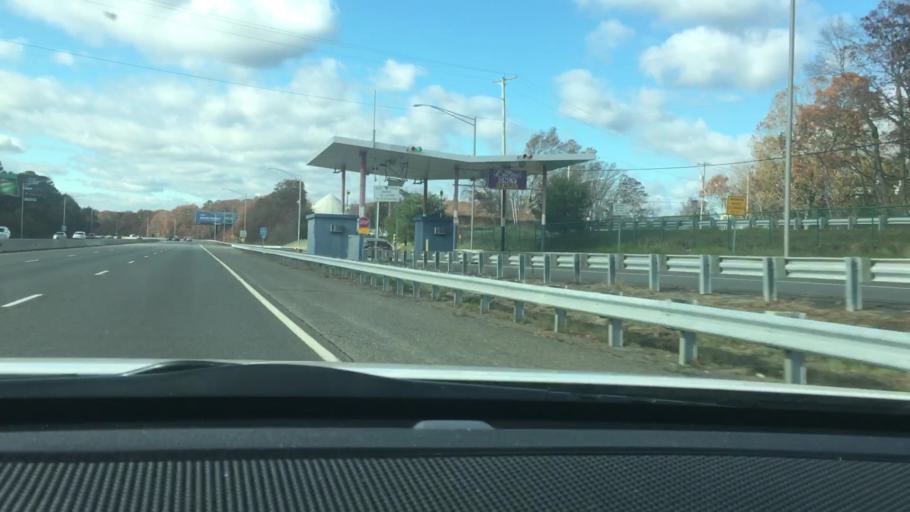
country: US
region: New Jersey
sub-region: Atlantic County
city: Pleasantville
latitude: 39.4032
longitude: -74.5259
